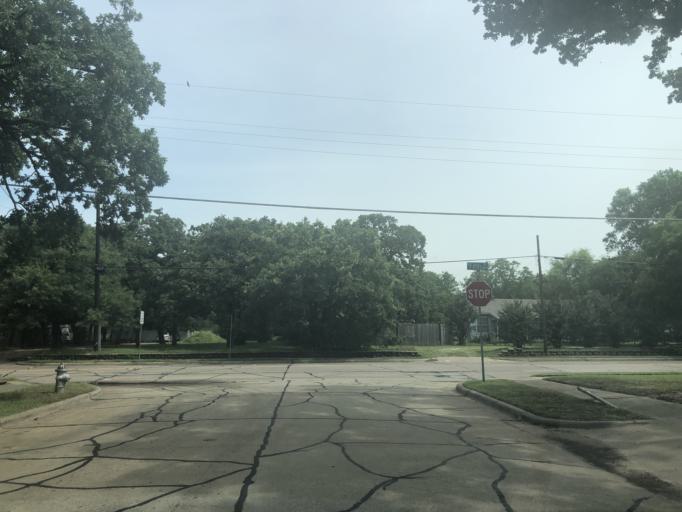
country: US
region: Texas
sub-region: Dallas County
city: Irving
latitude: 32.8093
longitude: -96.9742
